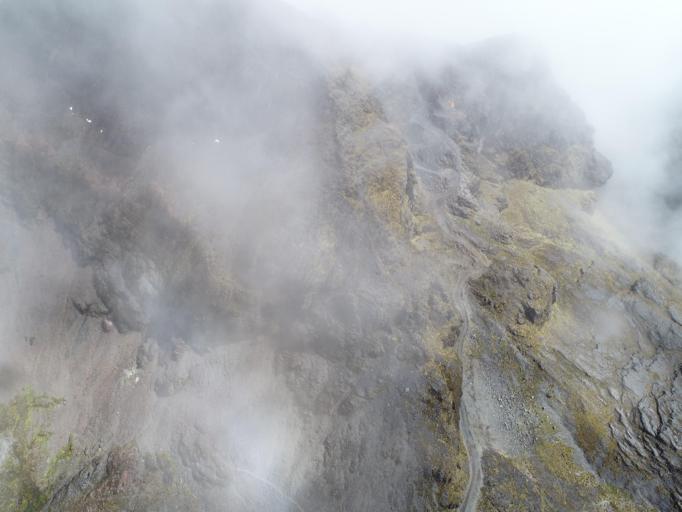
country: PE
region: Puno
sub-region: San Antonio De Putina
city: Sina
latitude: -14.7399
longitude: -69.0504
